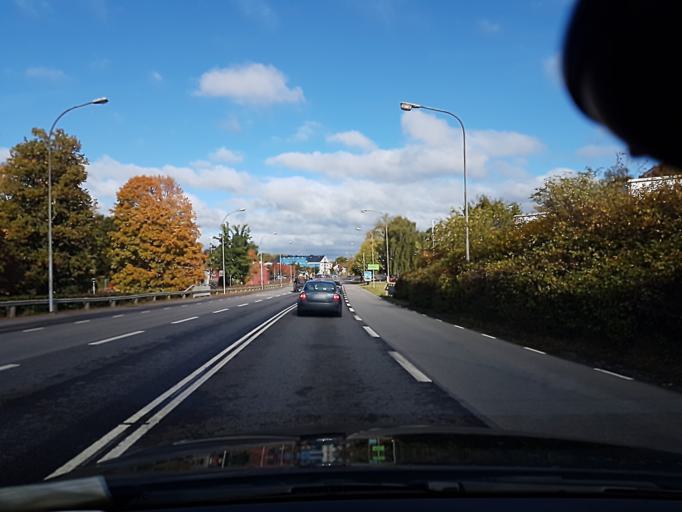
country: SE
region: Kronoberg
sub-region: Vaxjo Kommun
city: Vaexjoe
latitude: 56.8758
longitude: 14.8155
